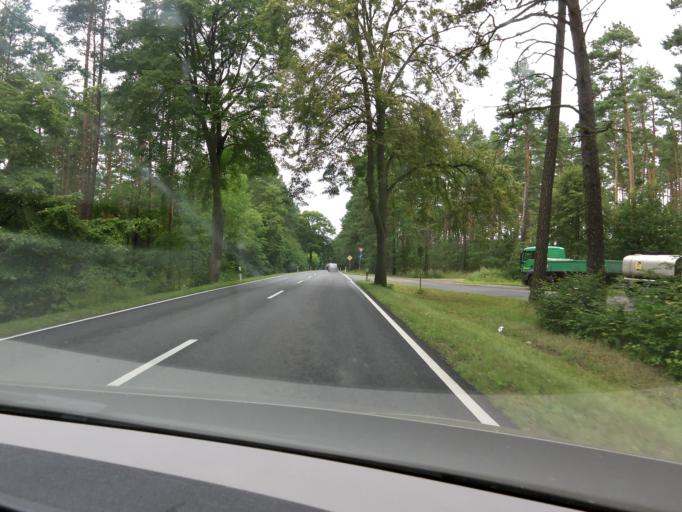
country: DE
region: Brandenburg
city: Furstenberg
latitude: 53.2179
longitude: 13.1251
